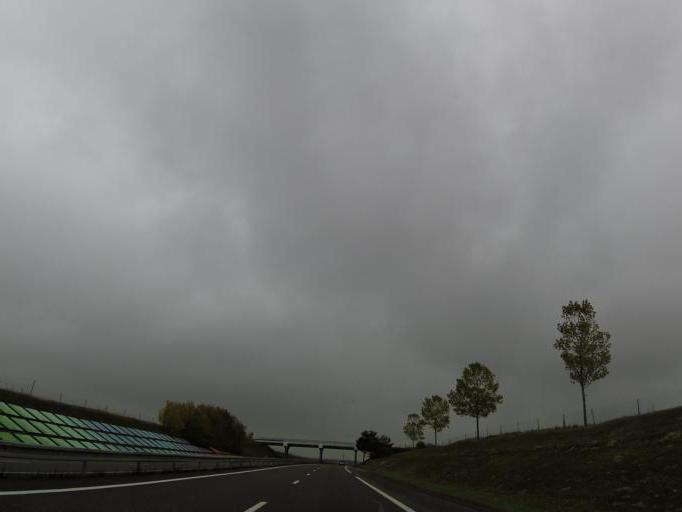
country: FR
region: Champagne-Ardenne
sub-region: Departement de la Marne
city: Suippes
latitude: 49.0551
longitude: 4.6850
